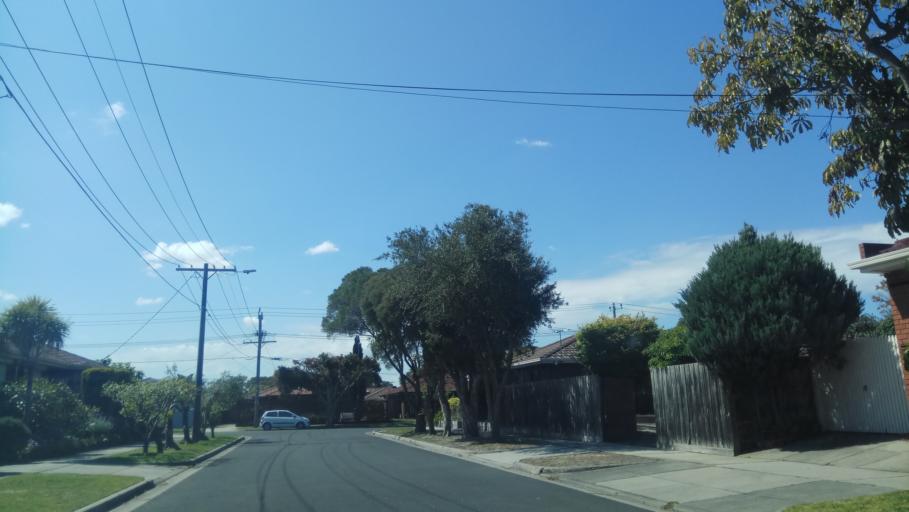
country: AU
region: Victoria
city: Heatherton
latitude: -37.9674
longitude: 145.0822
